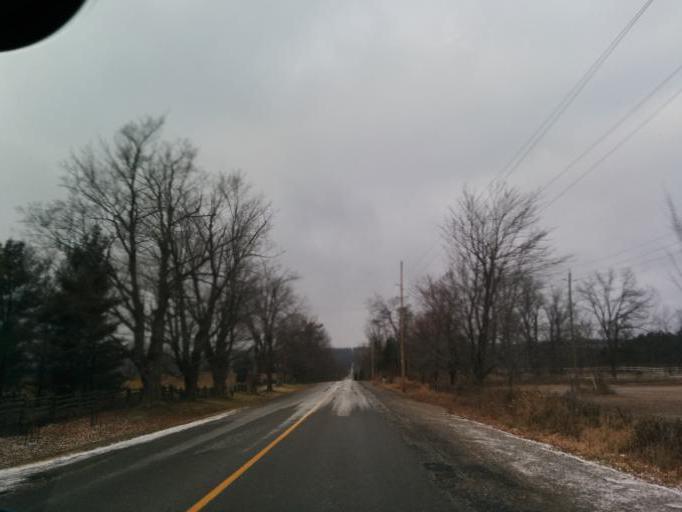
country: CA
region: Ontario
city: Orangeville
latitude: 43.8037
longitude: -79.9433
